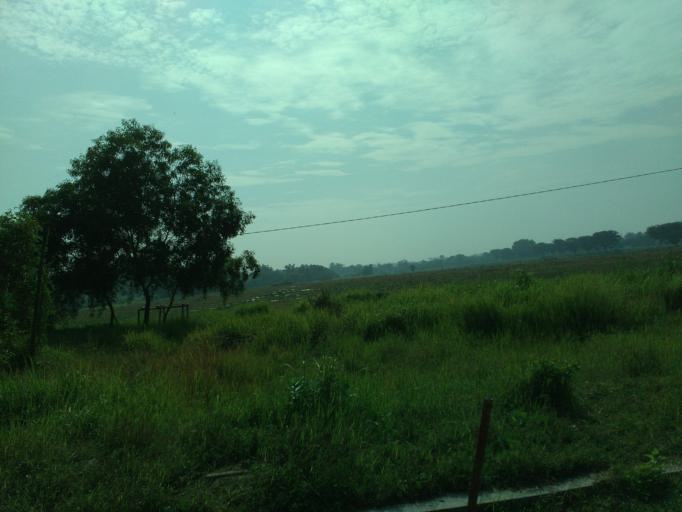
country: ID
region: Central Java
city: Delanggu
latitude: -7.6329
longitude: 110.6933
